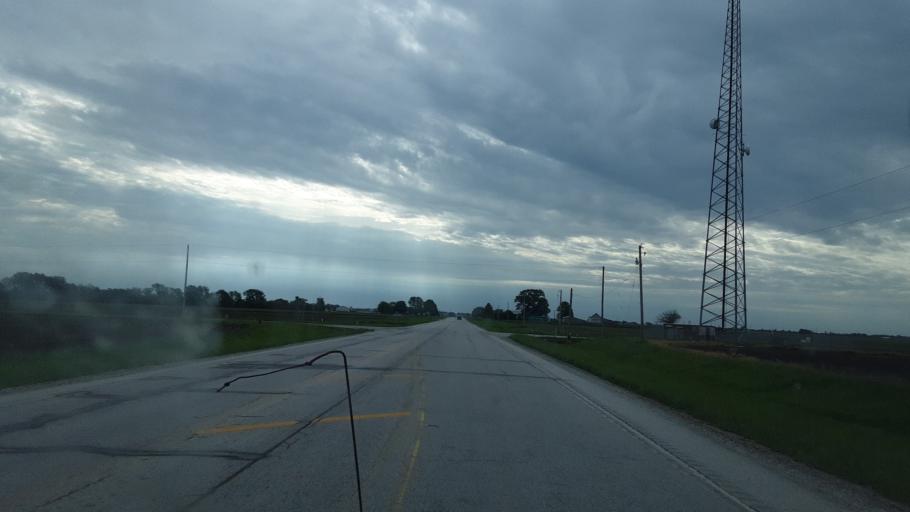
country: US
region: Illinois
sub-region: Hancock County
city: Hamilton
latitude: 40.3960
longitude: -91.3119
